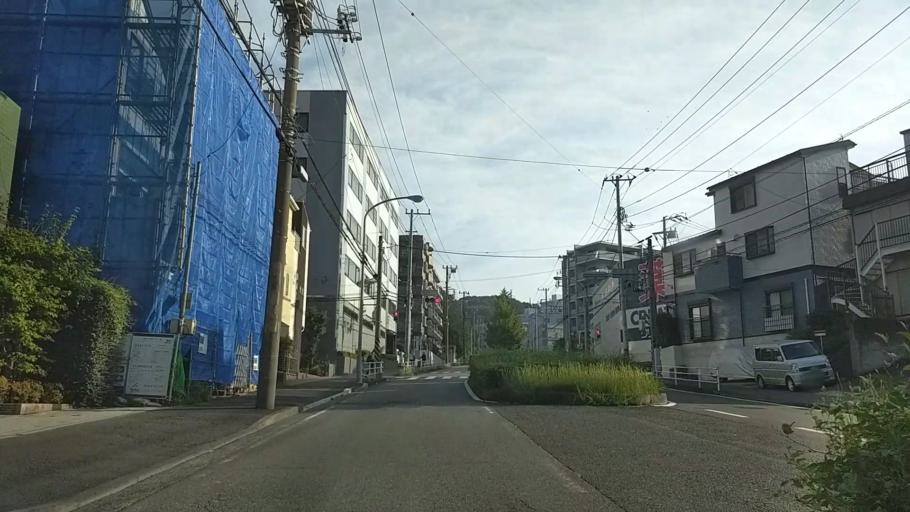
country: JP
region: Kanagawa
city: Yokohama
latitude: 35.4333
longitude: 139.5583
